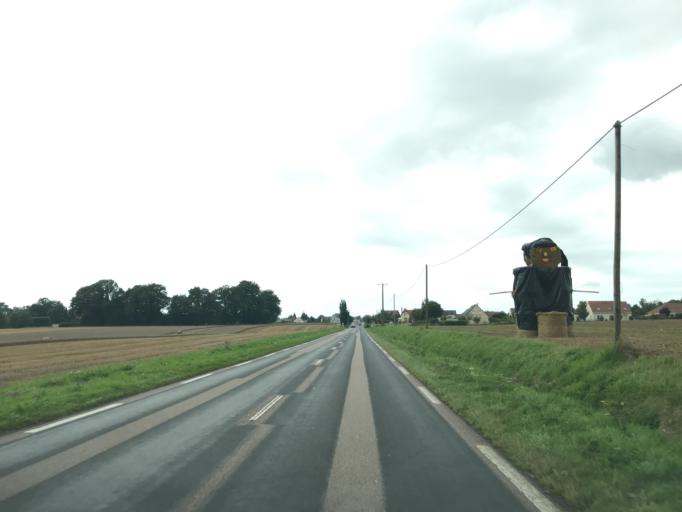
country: FR
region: Haute-Normandie
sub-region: Departement de la Seine-Maritime
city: Breaute
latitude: 49.6226
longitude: 0.4020
